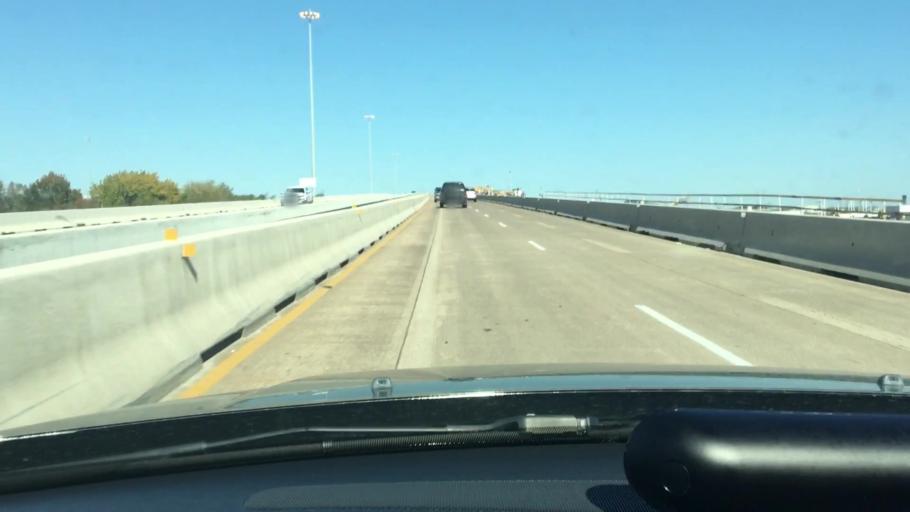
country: US
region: Texas
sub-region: Harris County
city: Deer Park
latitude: 29.7077
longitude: -95.1535
